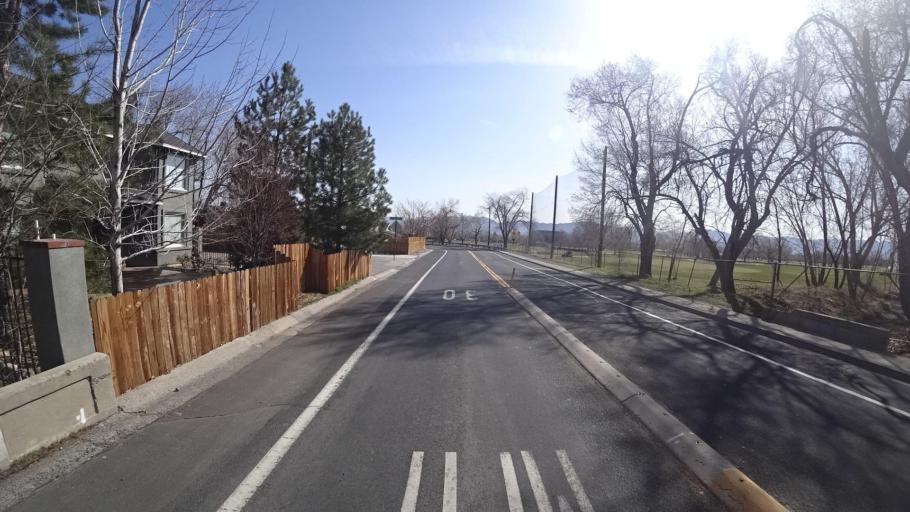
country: US
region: Nevada
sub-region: Washoe County
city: Reno
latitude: 39.5007
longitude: -119.8181
